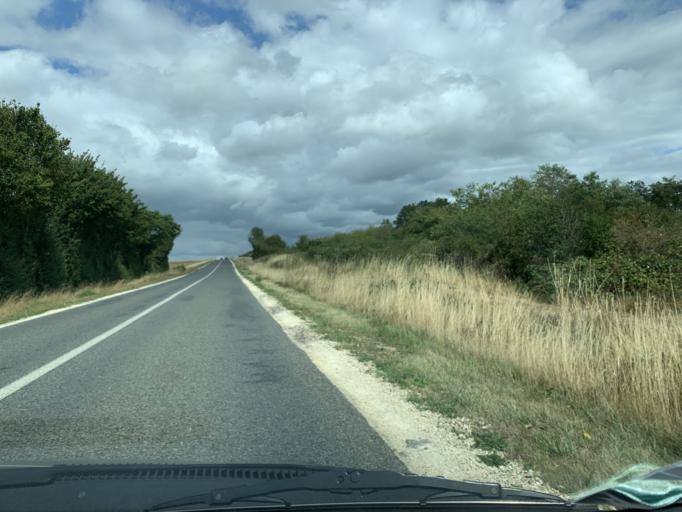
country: FR
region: Bourgogne
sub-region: Departement de la Nievre
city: Clamecy
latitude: 47.4347
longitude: 3.4845
